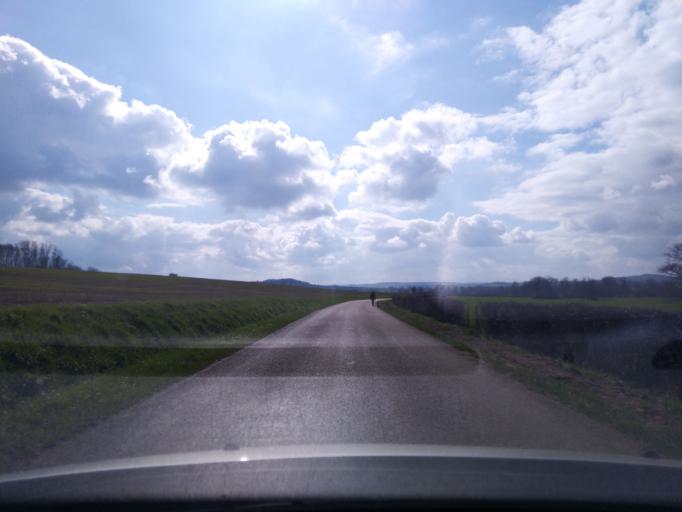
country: FR
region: Bourgogne
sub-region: Departement de l'Yonne
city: Avallon
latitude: 47.5572
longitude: 4.0585
